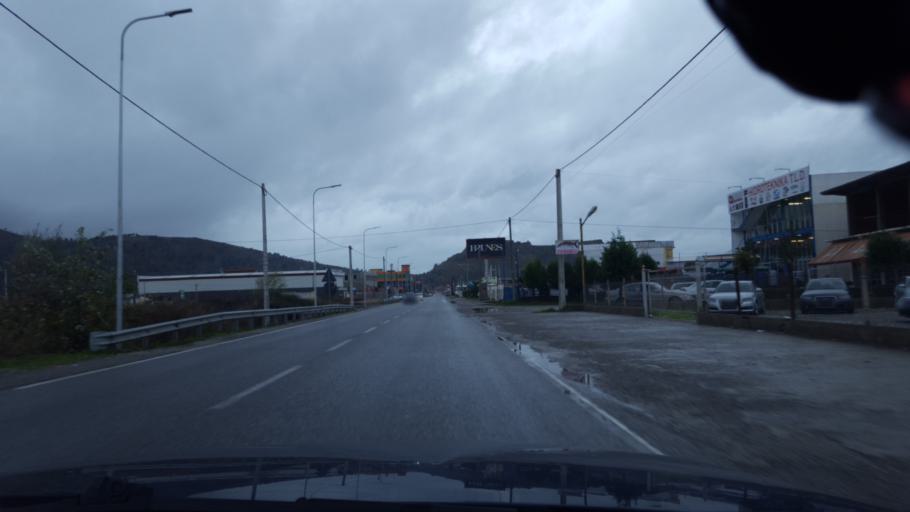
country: AL
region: Shkoder
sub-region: Rrethi i Malesia e Madhe
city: Kuc
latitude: 42.0336
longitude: 19.5017
